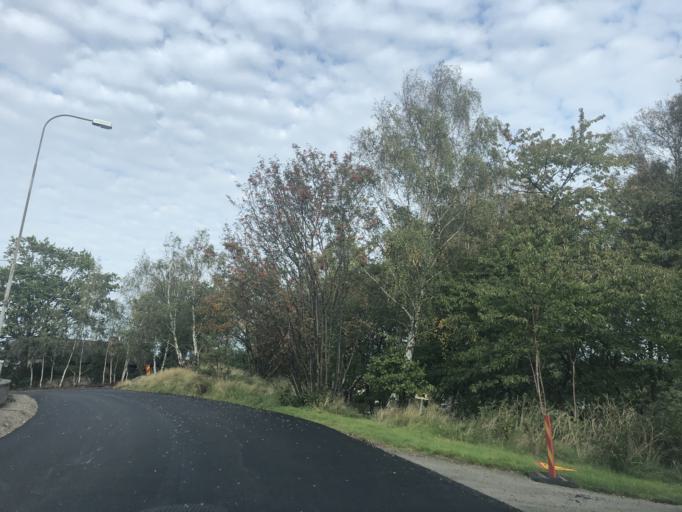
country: SE
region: Vaestra Goetaland
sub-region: Goteborg
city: Majorna
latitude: 57.6602
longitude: 11.8871
